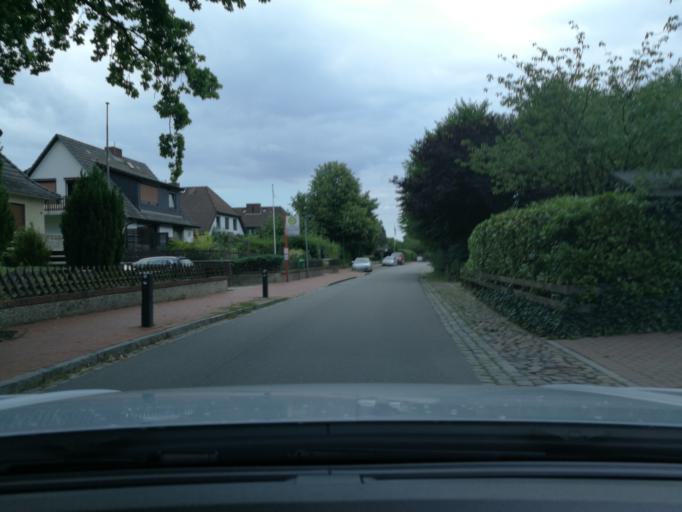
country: DE
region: Schleswig-Holstein
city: Wohltorf
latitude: 53.5458
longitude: 10.2771
